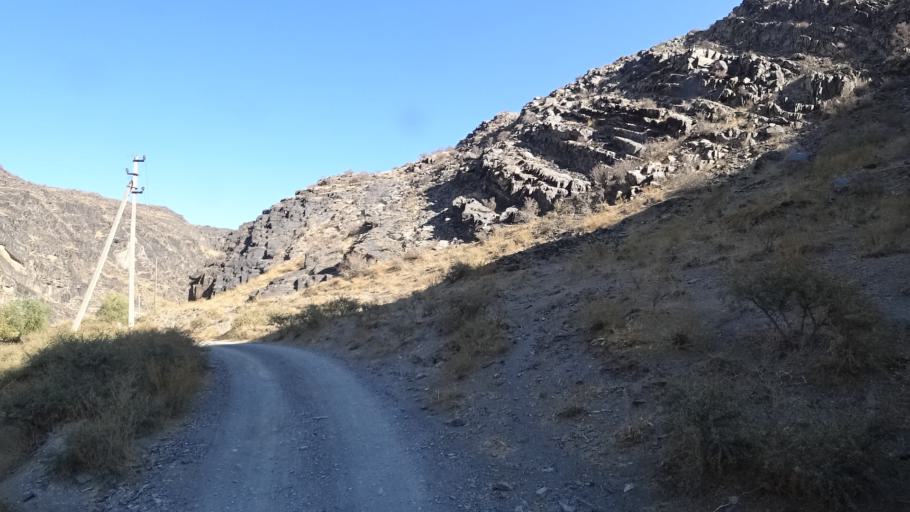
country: UZ
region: Navoiy
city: Nurota
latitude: 40.3048
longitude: 65.6173
